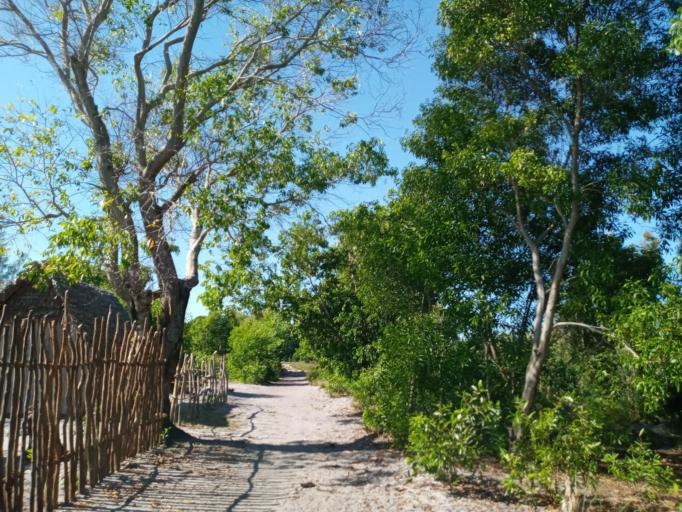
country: MG
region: Anosy
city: Fort Dauphin
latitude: -24.9056
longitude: 47.0988
